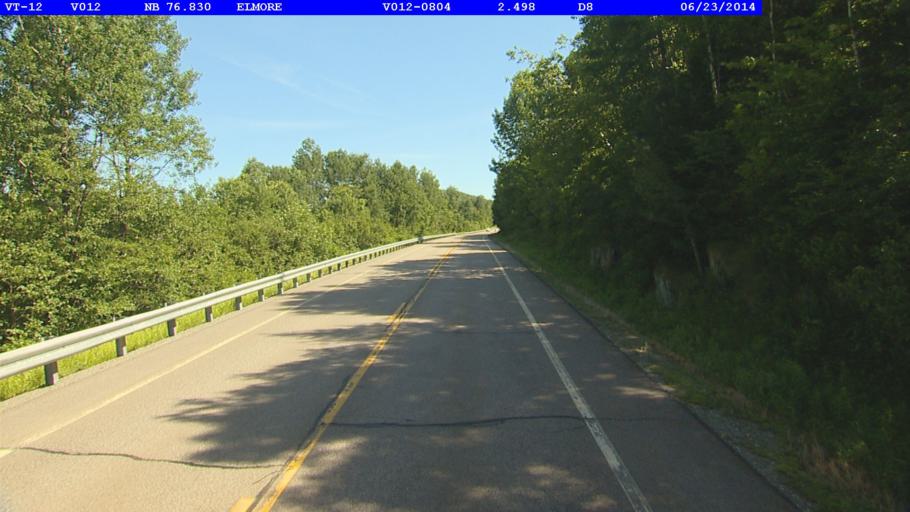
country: US
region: Vermont
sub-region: Lamoille County
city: Morrisville
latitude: 44.4829
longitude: -72.5271
